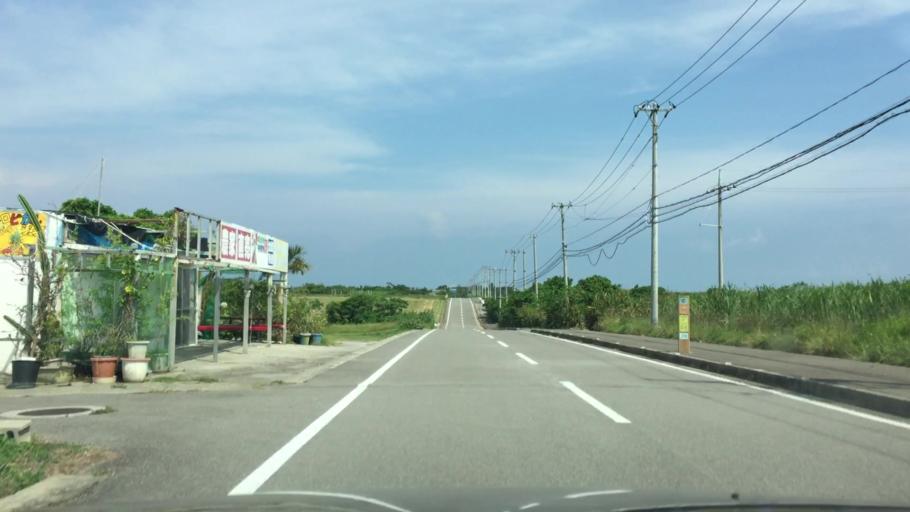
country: JP
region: Okinawa
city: Ishigaki
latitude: 24.5051
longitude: 124.2738
